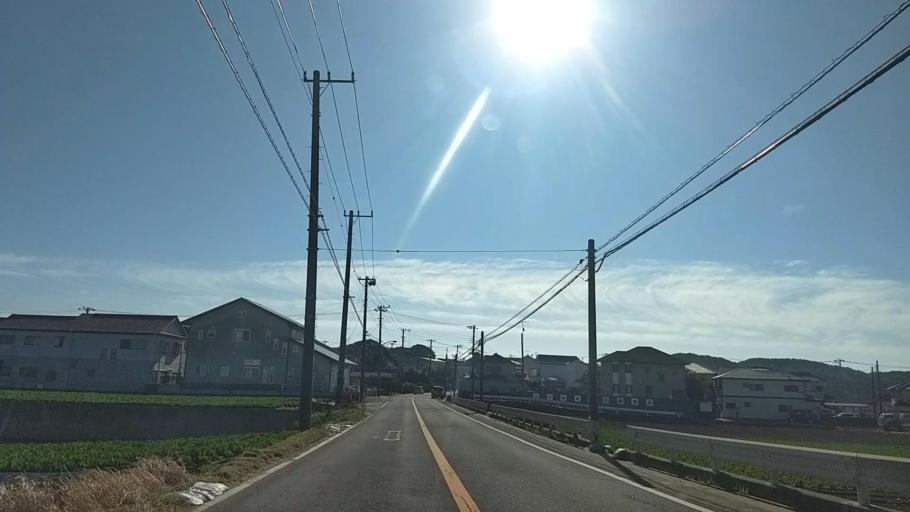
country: JP
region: Chiba
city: Hasaki
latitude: 35.7126
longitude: 140.8594
